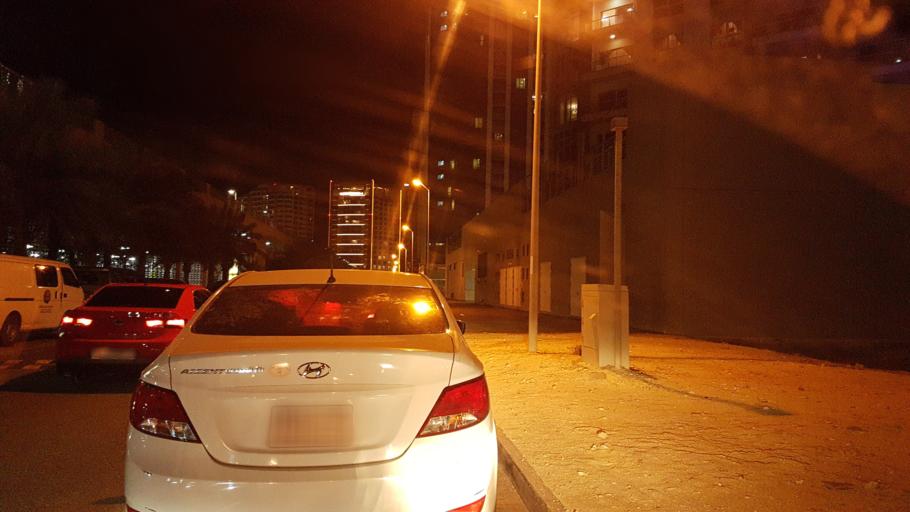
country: BH
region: Muharraq
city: Al Hadd
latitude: 26.2860
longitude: 50.6639
